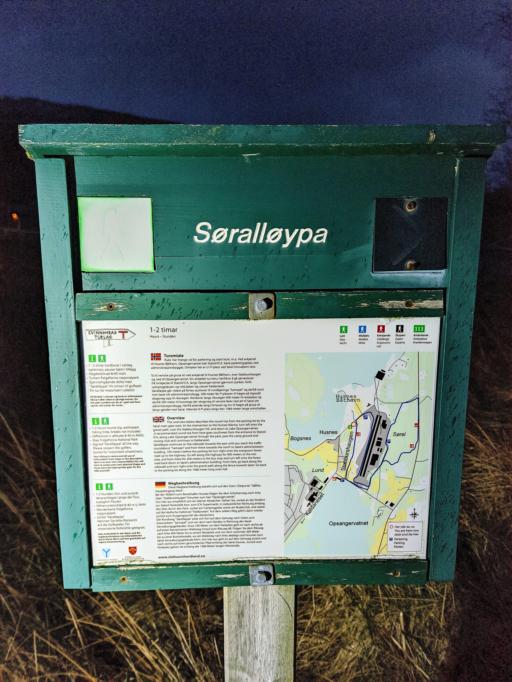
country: NO
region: Hordaland
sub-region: Etne
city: Etne
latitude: 59.8697
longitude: 5.7636
